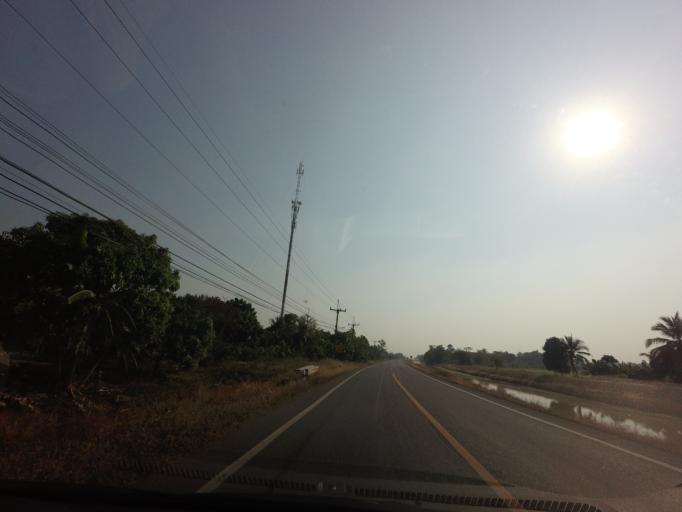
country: TH
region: Chachoengsao
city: Khlong Khuean
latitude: 13.7964
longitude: 101.1778
